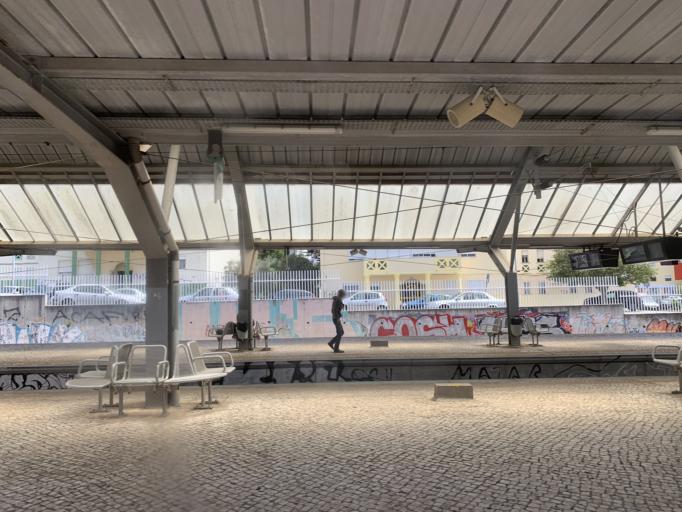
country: PT
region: Lisbon
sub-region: Sintra
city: Rio de Mouro
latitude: 38.7936
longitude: -9.3312
